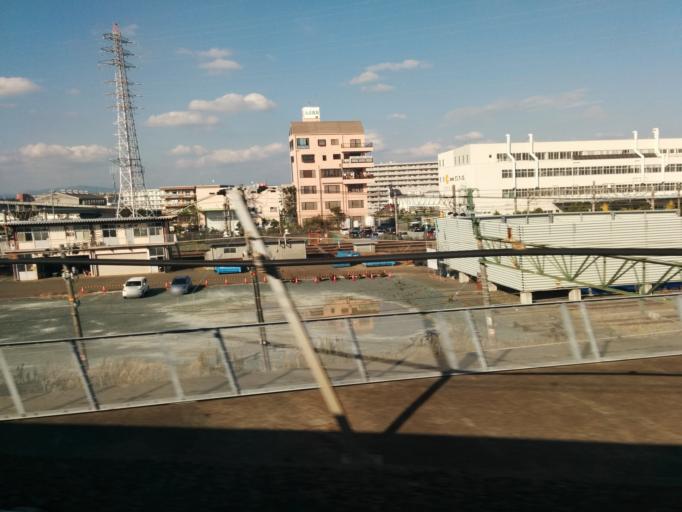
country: JP
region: Shizuoka
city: Hamamatsu
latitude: 34.6926
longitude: 137.7084
